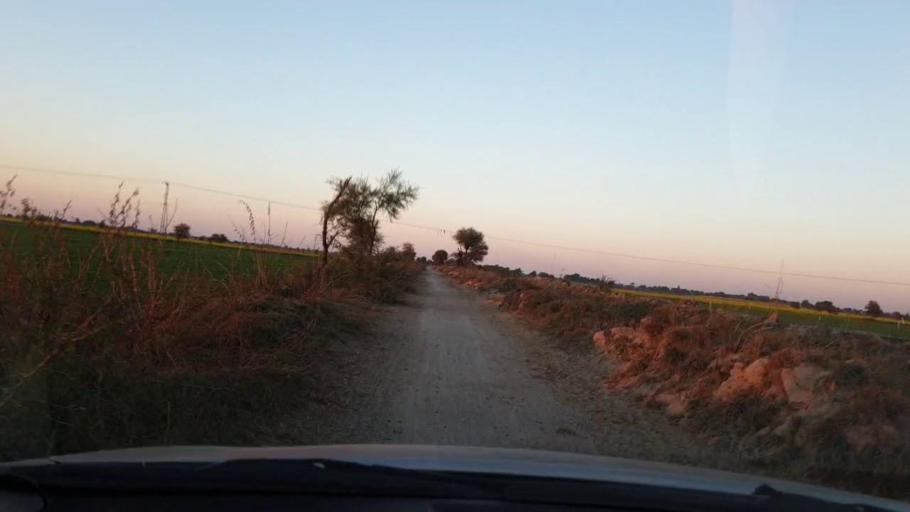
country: PK
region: Sindh
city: Jhol
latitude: 25.9047
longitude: 68.8860
